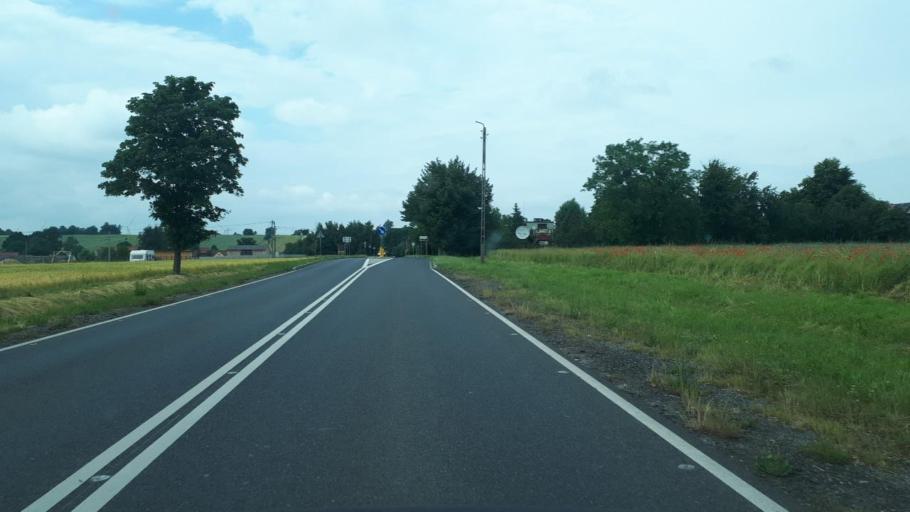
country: PL
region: Silesian Voivodeship
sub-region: Powiat gliwicki
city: Wielowies
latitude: 50.4729
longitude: 18.6093
